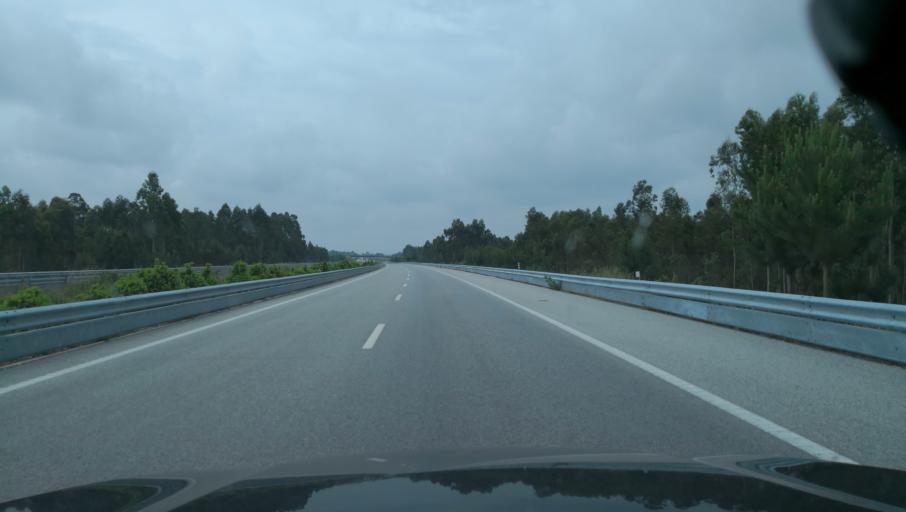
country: PT
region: Coimbra
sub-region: Figueira da Foz
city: Alhadas
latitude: 40.2722
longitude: -8.7591
